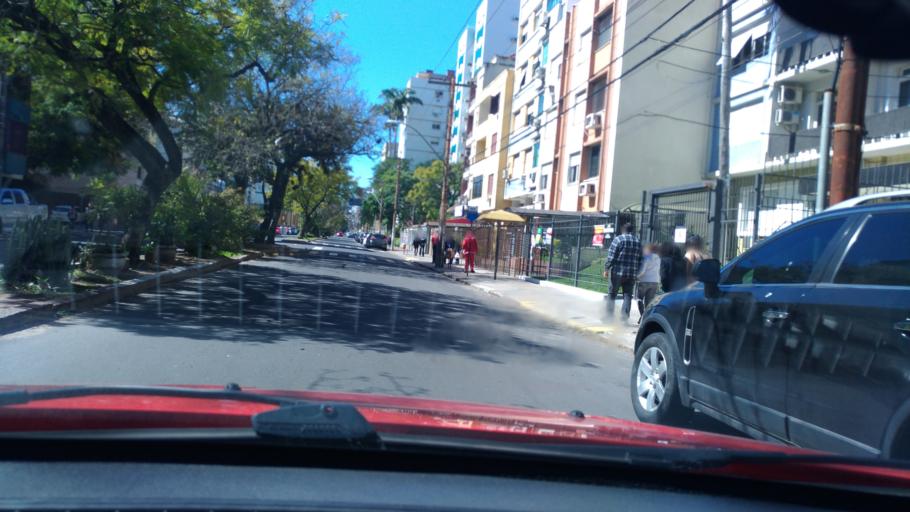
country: BR
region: Rio Grande do Sul
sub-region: Porto Alegre
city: Porto Alegre
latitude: -30.0407
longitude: -51.2155
